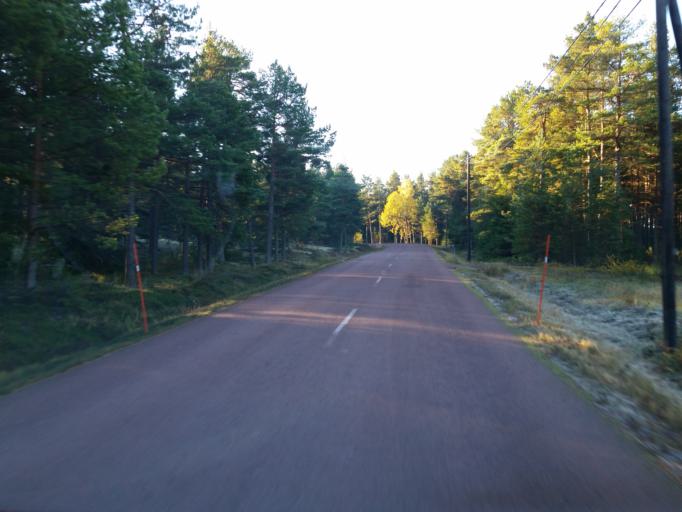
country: AX
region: Alands skaergard
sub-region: Vardoe
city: Vardoe
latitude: 60.2921
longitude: 20.3869
